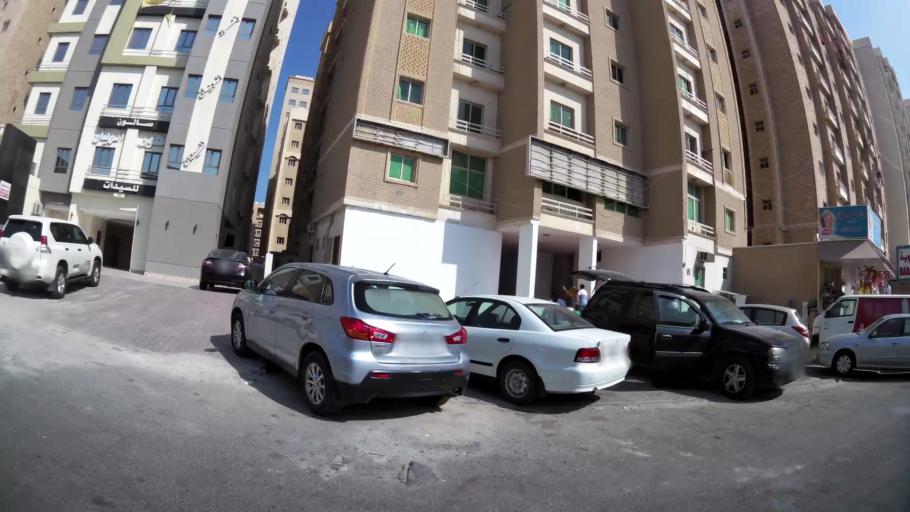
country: KW
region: Al Ahmadi
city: Al Fahahil
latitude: 29.0817
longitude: 48.1231
